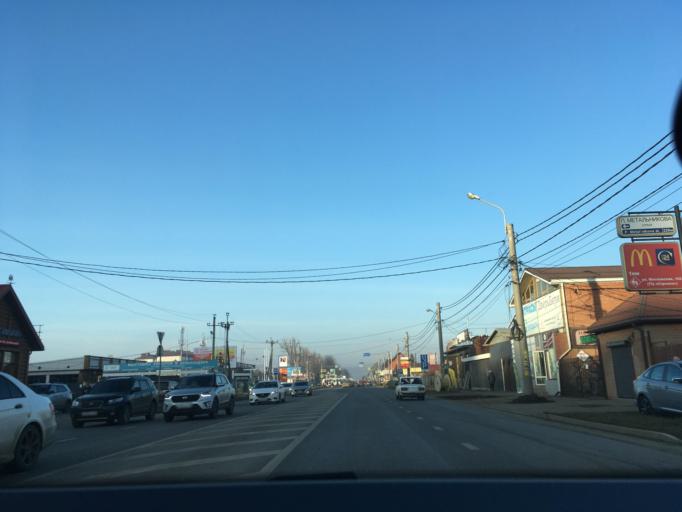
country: RU
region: Krasnodarskiy
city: Krasnodar
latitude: 45.0925
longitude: 39.0140
